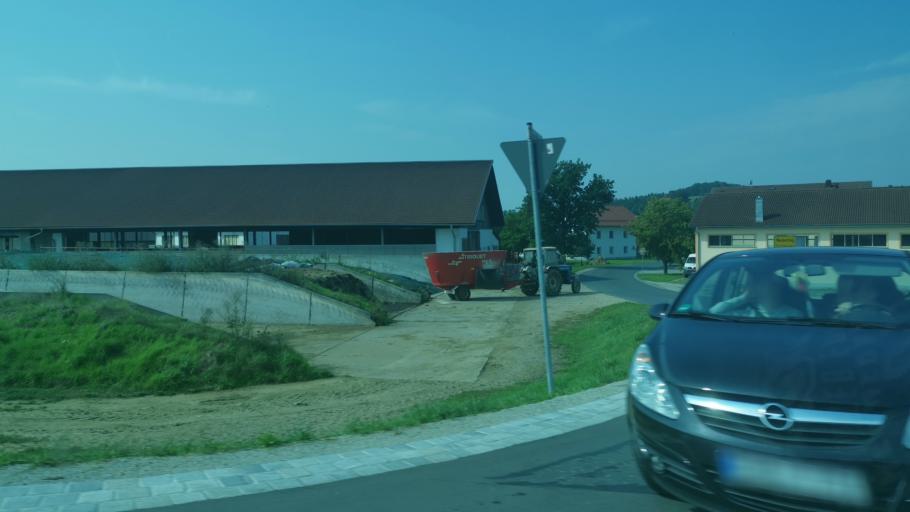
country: DE
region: Bavaria
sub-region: Upper Palatinate
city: Willmering
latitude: 49.2468
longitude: 12.6535
